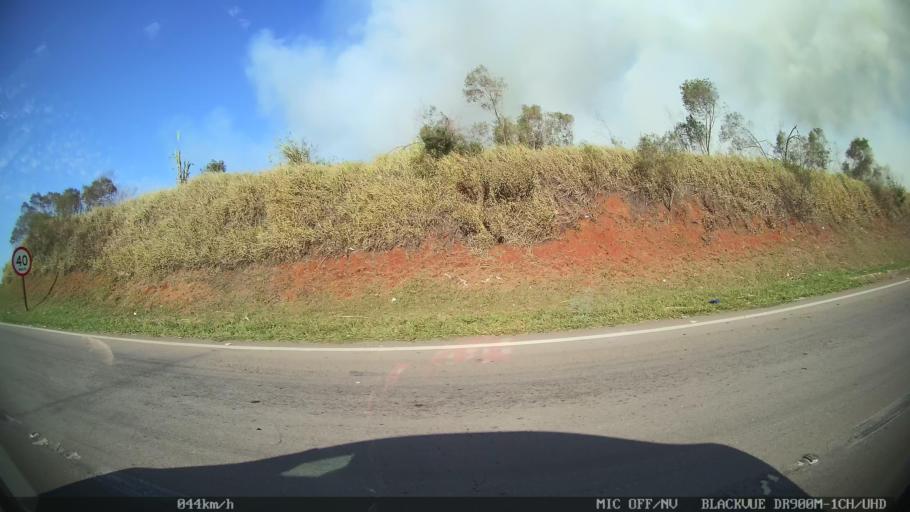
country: BR
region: Sao Paulo
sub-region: Piracicaba
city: Piracicaba
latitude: -22.6952
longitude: -47.6033
